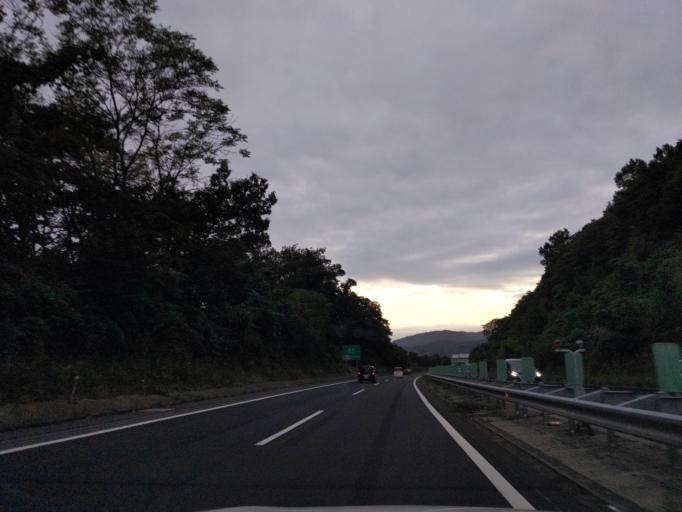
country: JP
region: Fukushima
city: Yanagawamachi-saiwaicho
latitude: 37.8856
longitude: 140.5440
